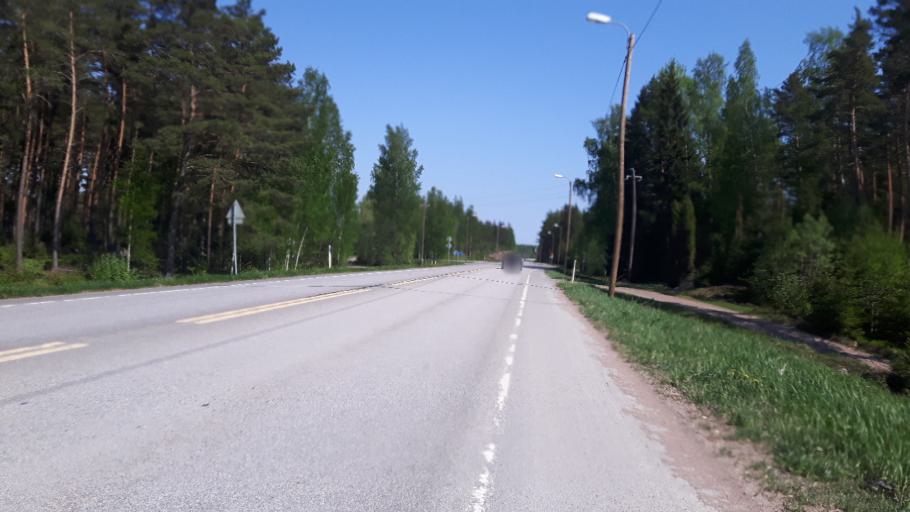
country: FI
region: Kymenlaakso
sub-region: Kotka-Hamina
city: Broby
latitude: 60.4905
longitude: 26.6874
